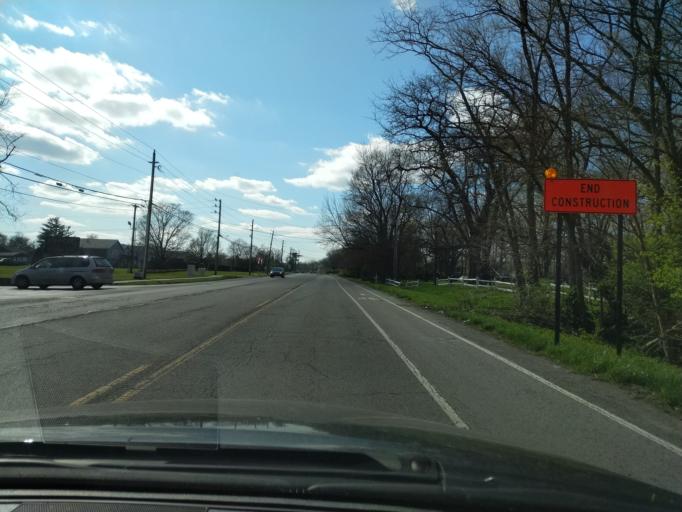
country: US
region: Indiana
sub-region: Marion County
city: Meridian Hills
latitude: 39.8856
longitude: -86.1944
